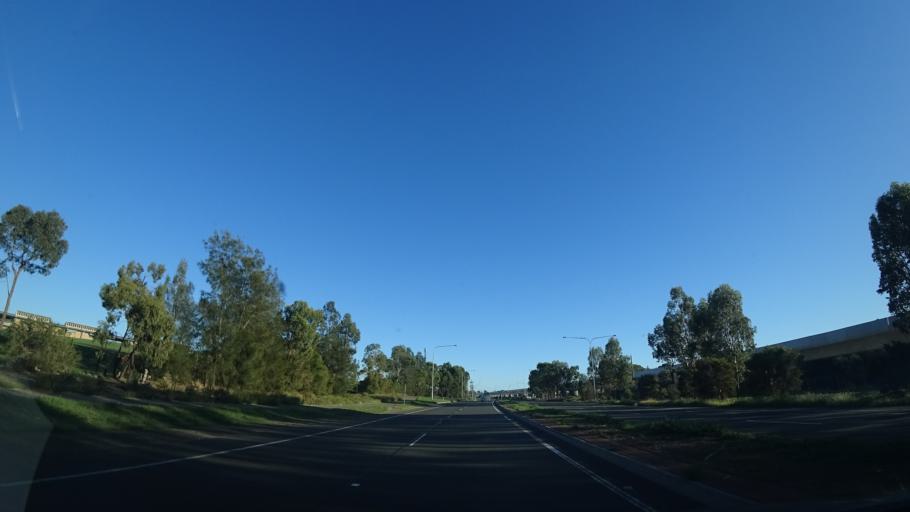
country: AU
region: New South Wales
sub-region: Blacktown
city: Stanhope Gardens
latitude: -33.7068
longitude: 150.9309
